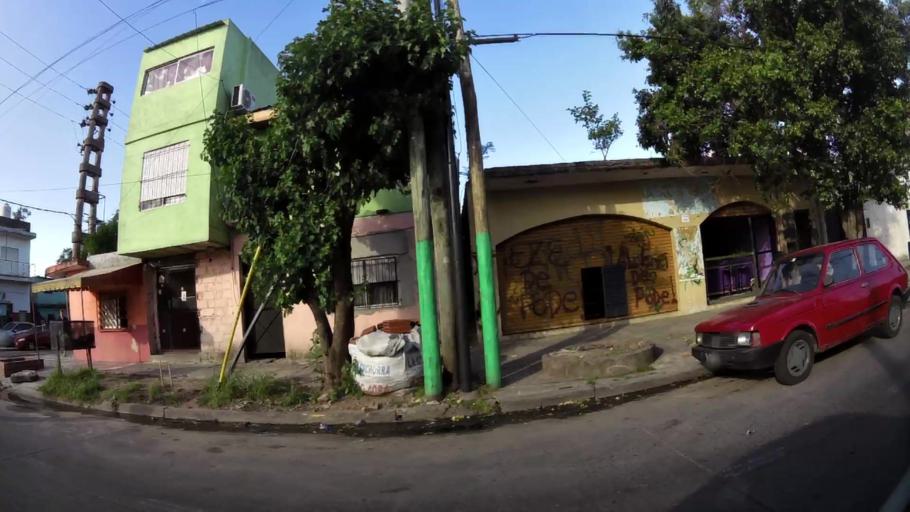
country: AR
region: Buenos Aires
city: Hurlingham
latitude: -34.5758
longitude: -58.6088
